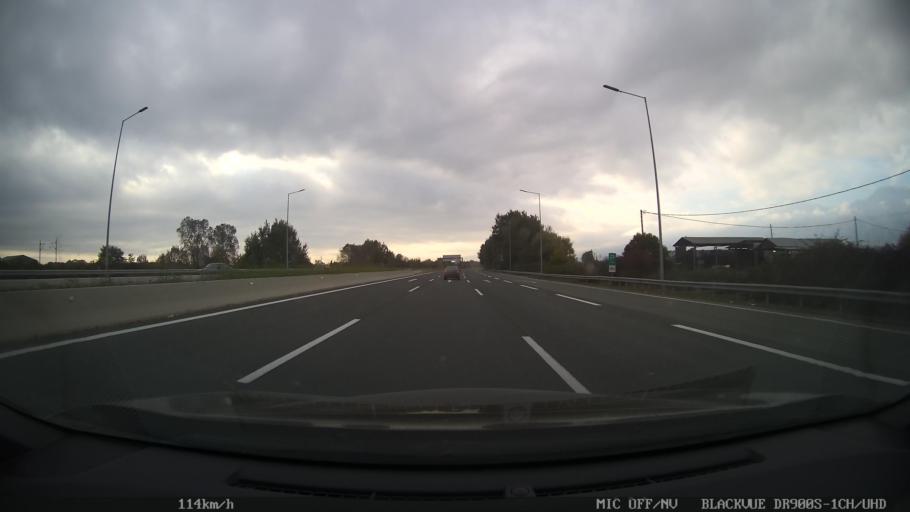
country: GR
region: Central Macedonia
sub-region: Nomos Pierias
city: Nea Efesos
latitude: 40.1884
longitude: 22.5504
